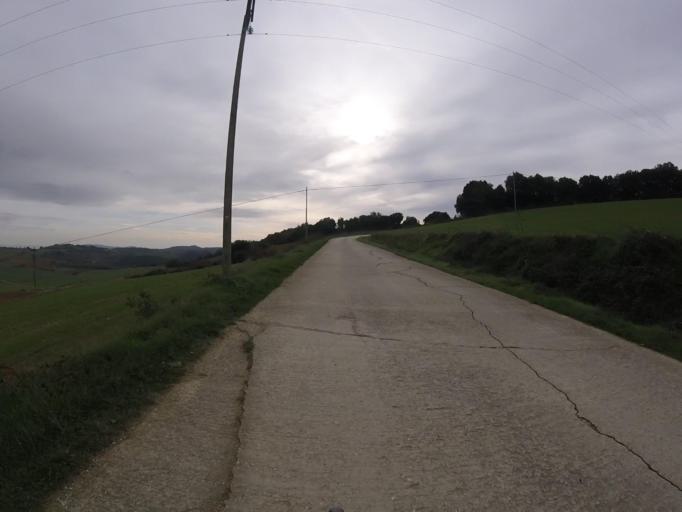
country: ES
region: Navarre
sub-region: Provincia de Navarra
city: Estella
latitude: 42.7176
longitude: -2.0433
